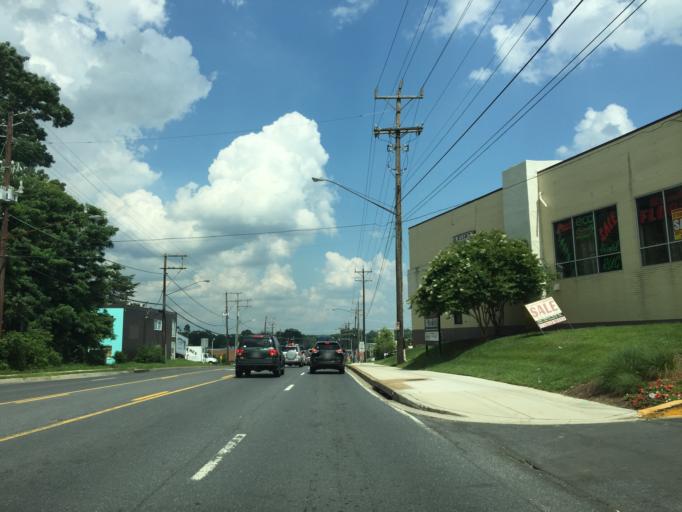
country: US
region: Maryland
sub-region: Montgomery County
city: North Bethesda
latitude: 39.0532
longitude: -77.1128
